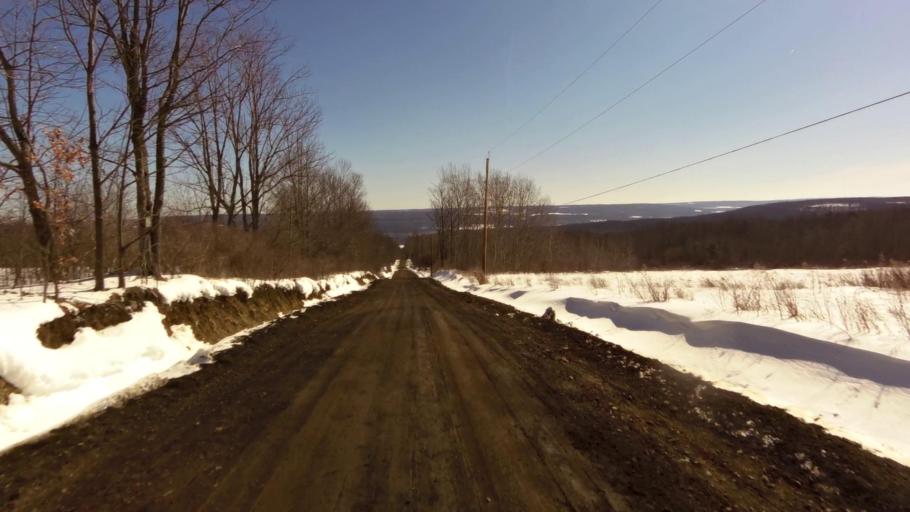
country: US
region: New York
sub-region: Allegany County
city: Houghton
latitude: 42.3593
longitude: -78.1717
